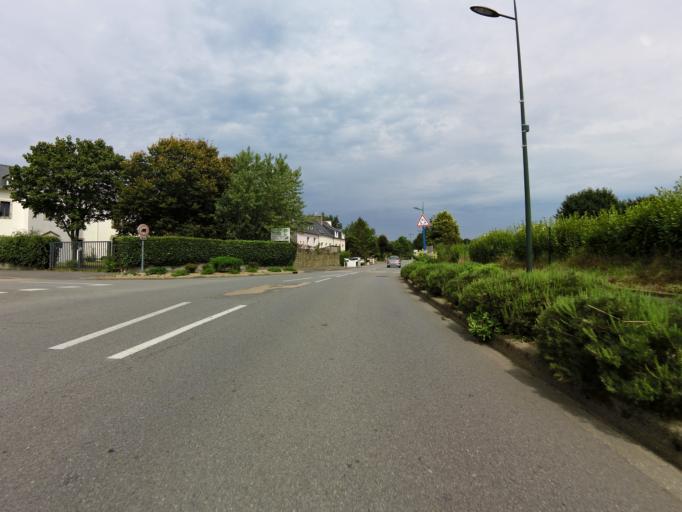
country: FR
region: Brittany
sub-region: Departement du Finistere
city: Poullan-sur-Mer
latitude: 48.0814
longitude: -4.4121
